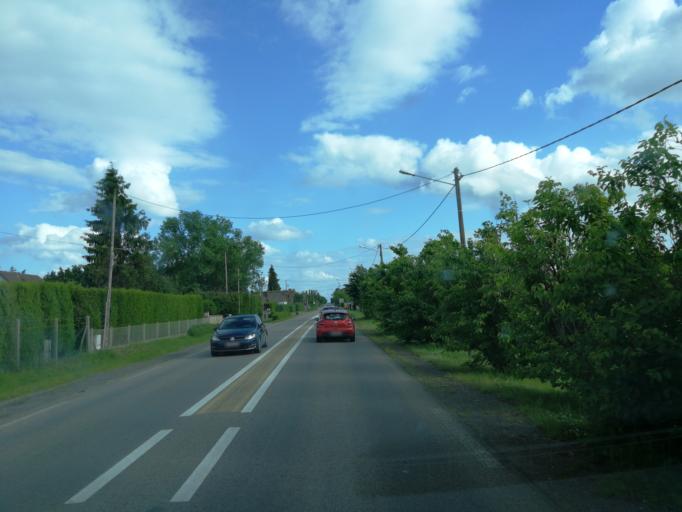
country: FR
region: Haute-Normandie
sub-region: Departement de l'Eure
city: Le Neubourg
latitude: 49.1230
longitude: 0.9096
